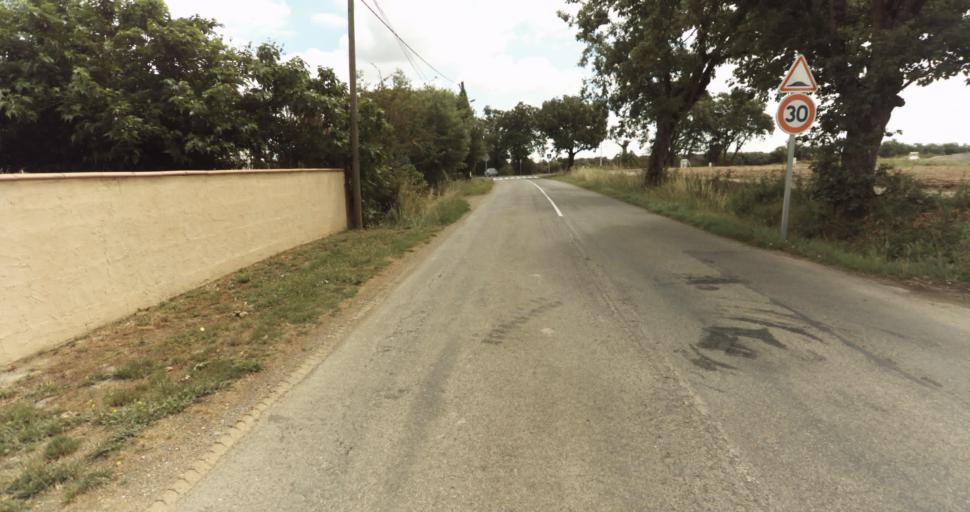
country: FR
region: Midi-Pyrenees
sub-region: Departement de la Haute-Garonne
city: Fontenilles
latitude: 43.5586
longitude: 1.1984
